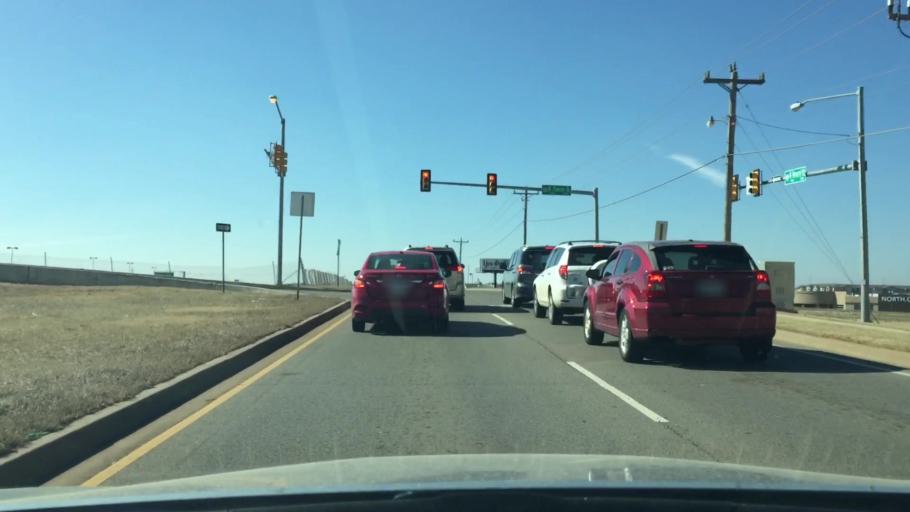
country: US
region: Oklahoma
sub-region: Oklahoma County
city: The Village
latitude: 35.6094
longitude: -97.5385
